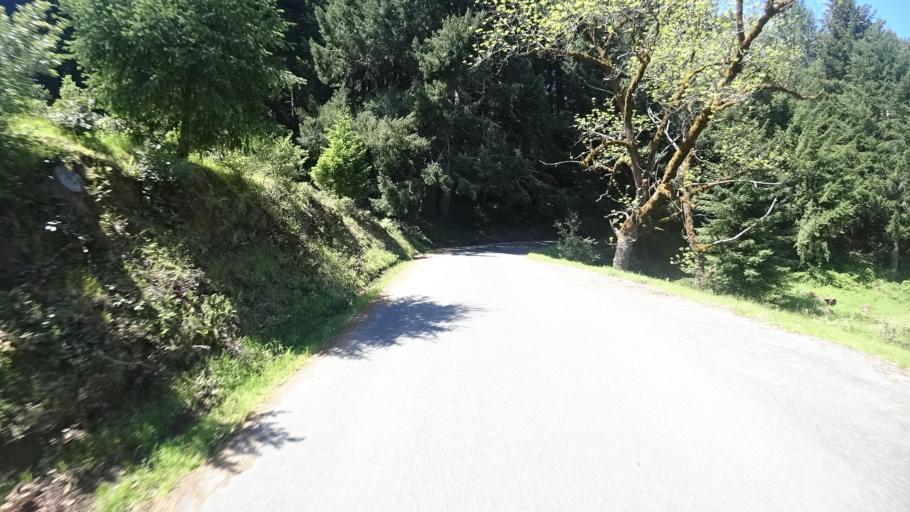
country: US
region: California
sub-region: Humboldt County
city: Redway
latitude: 40.1459
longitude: -124.0141
